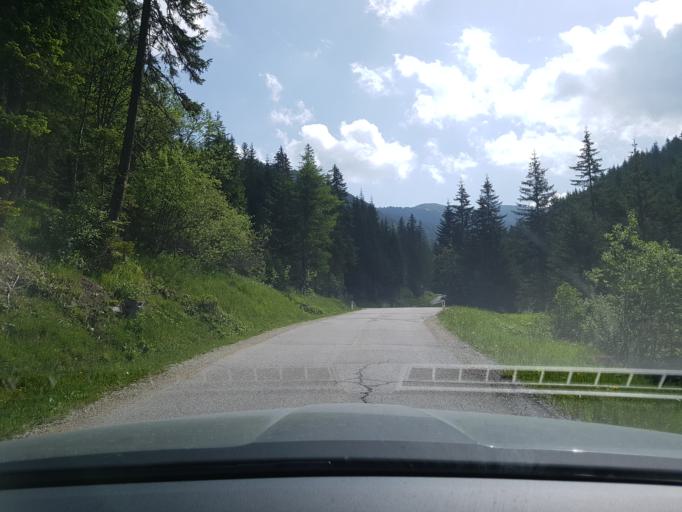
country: AT
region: Salzburg
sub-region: Politischer Bezirk Tamsweg
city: Thomatal
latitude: 47.0345
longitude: 13.7366
